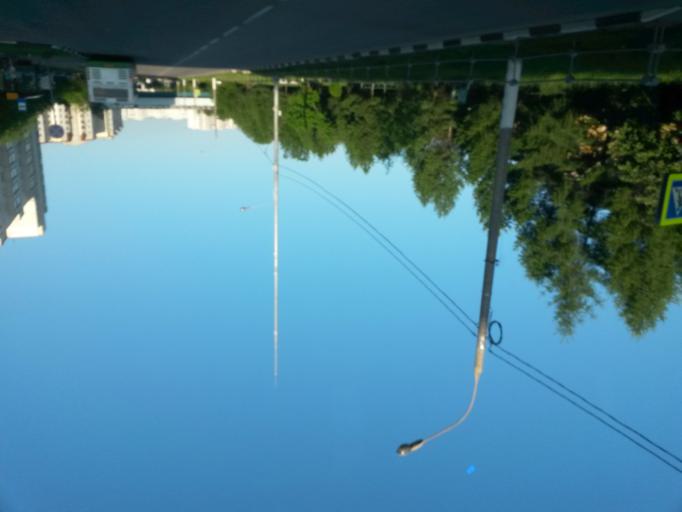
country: RU
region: Moscow
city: Annino
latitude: 55.5526
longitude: 37.5606
